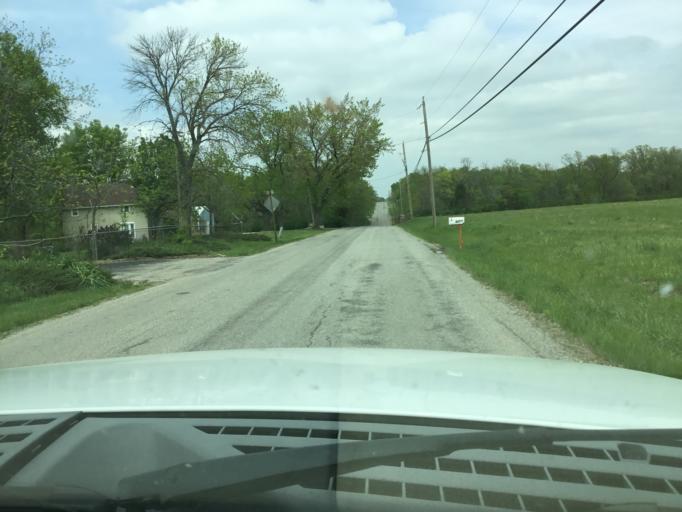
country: US
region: Kansas
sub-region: Shawnee County
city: Topeka
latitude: 38.9873
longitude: -95.5864
